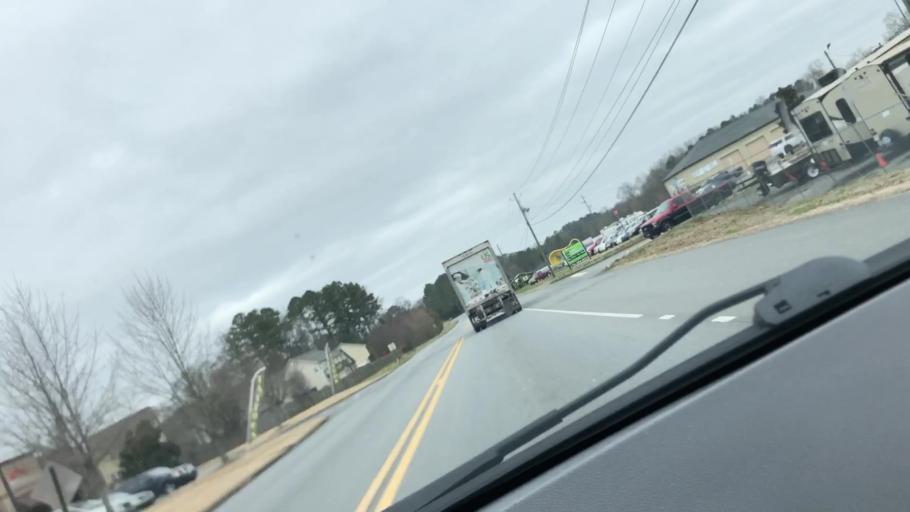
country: US
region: Georgia
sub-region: Bartow County
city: Cartersville
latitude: 34.1848
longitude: -84.8298
